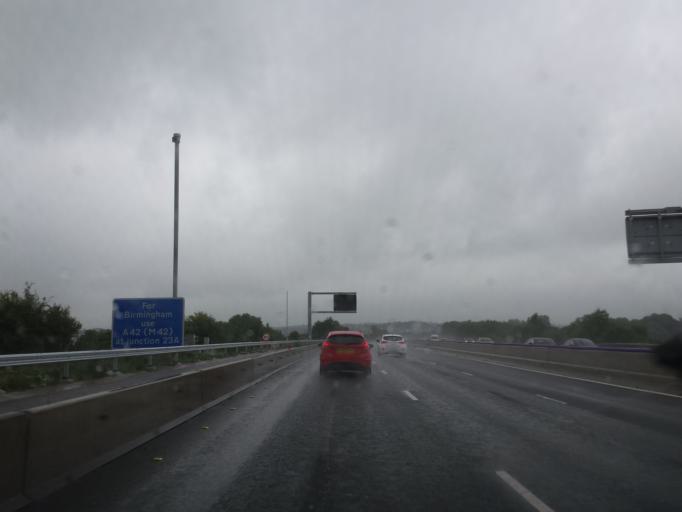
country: GB
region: England
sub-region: Derbyshire
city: Blackwell
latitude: 53.1268
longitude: -1.3297
